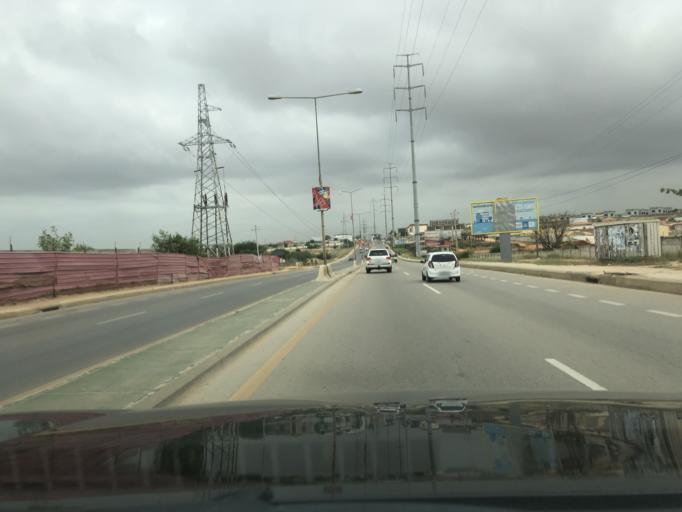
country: AO
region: Luanda
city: Luanda
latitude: -8.9690
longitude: 13.2074
